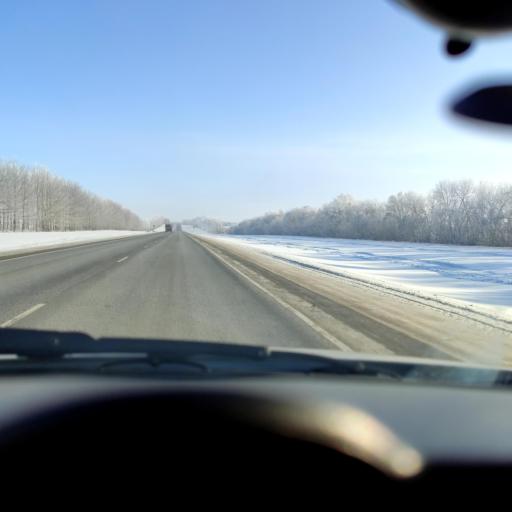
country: RU
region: Kursk
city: Kshenskiy
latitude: 51.6173
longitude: 37.7904
